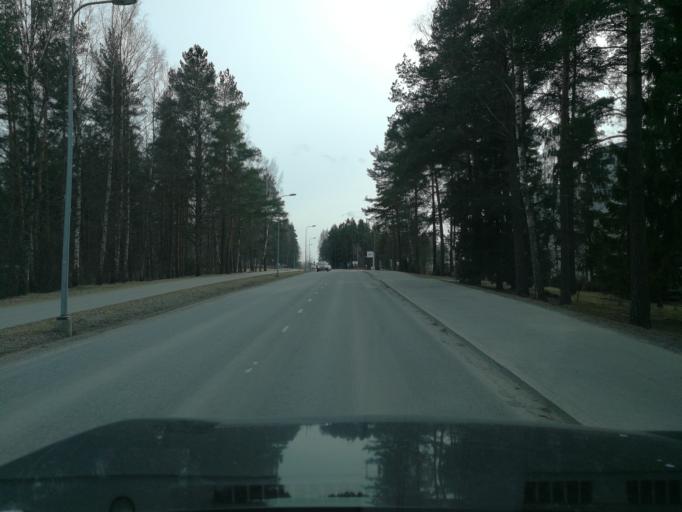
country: FI
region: Uusimaa
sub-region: Helsinki
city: Lohja
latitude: 60.1875
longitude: 23.9965
